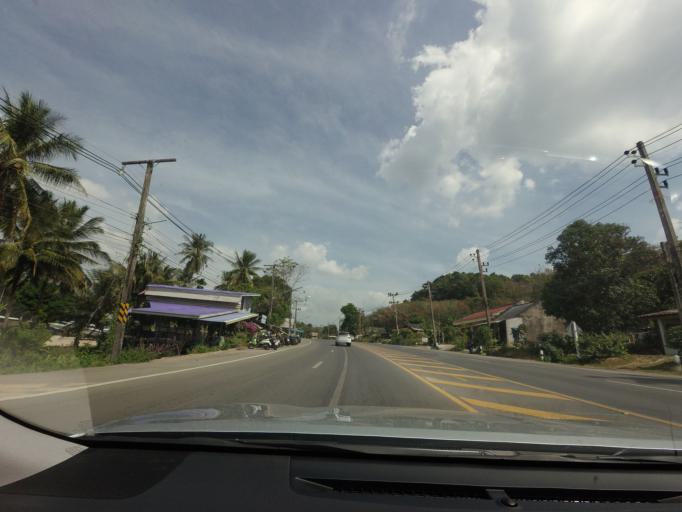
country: TH
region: Phangnga
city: Ban Ao Nang
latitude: 8.0522
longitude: 98.7683
